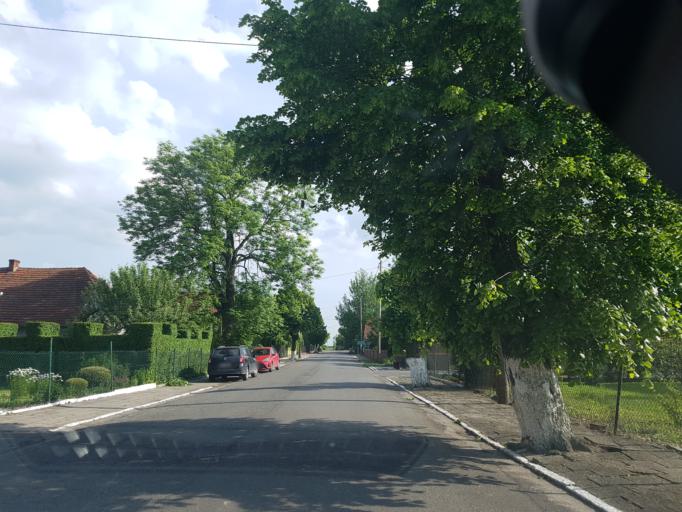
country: PL
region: Lower Silesian Voivodeship
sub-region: Powiat strzelinski
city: Wiazow
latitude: 50.8677
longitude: 17.1564
